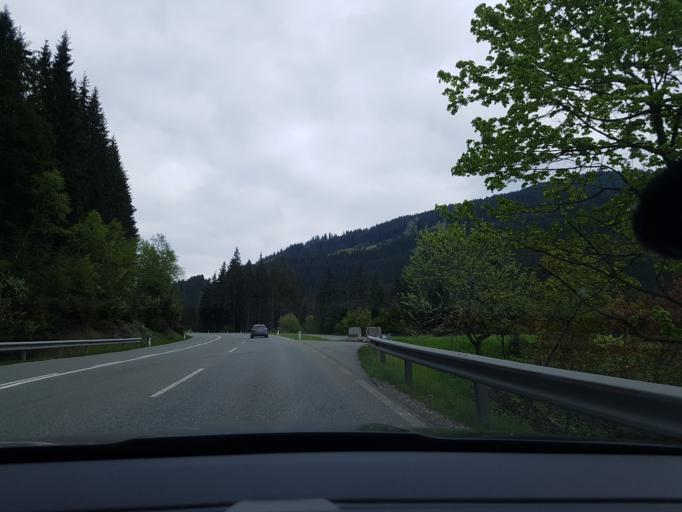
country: AT
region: Tyrol
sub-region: Politischer Bezirk Kitzbuhel
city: Jochberg
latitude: 47.3292
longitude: 12.4070
